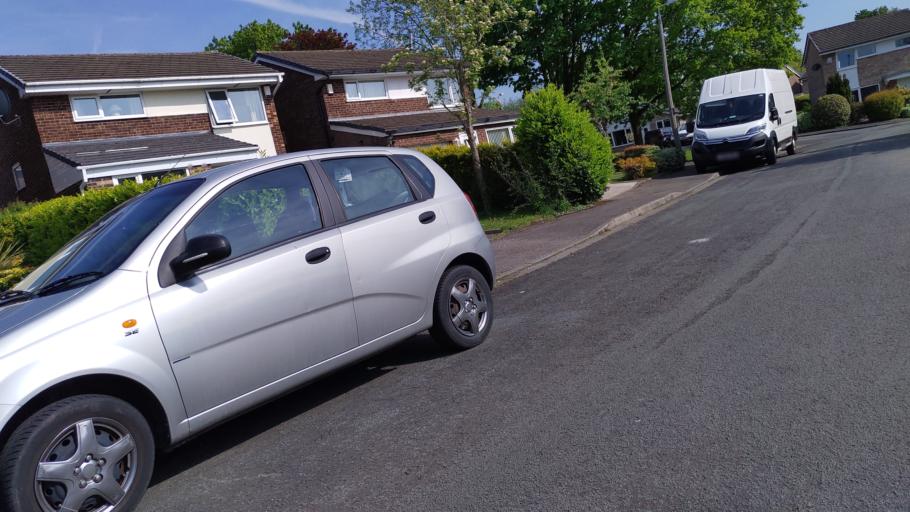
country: GB
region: England
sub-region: Lancashire
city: Chorley
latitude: 53.6642
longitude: -2.6384
